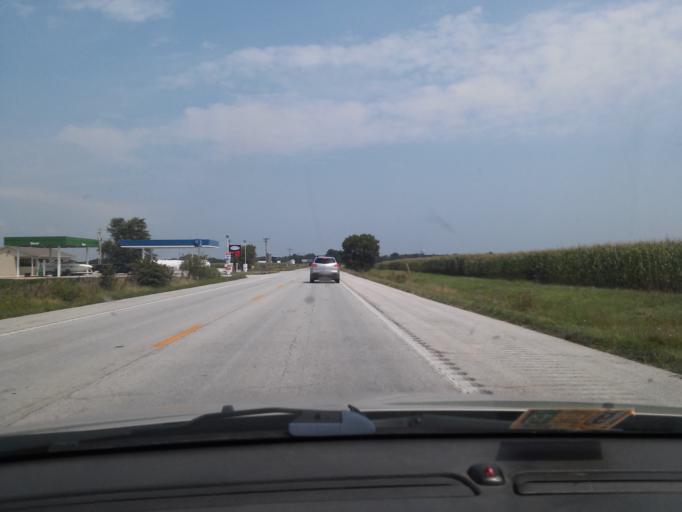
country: US
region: Missouri
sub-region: Montgomery County
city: Wellsville
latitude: 39.2273
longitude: -91.6460
